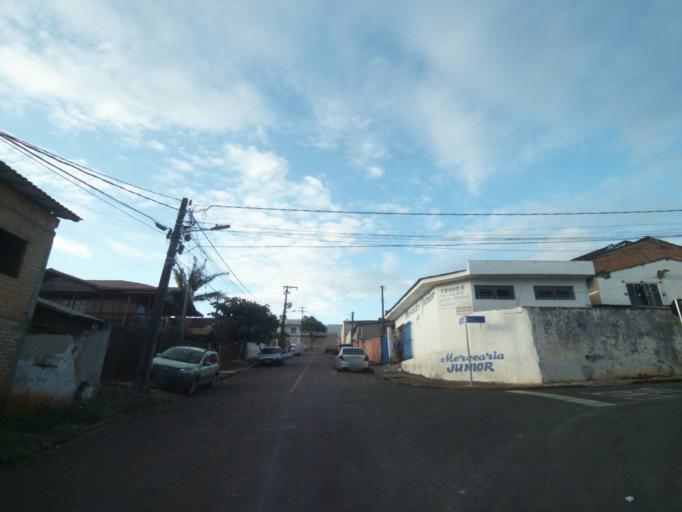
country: BR
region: Parana
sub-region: Telemaco Borba
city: Telemaco Borba
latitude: -24.3293
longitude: -50.6414
